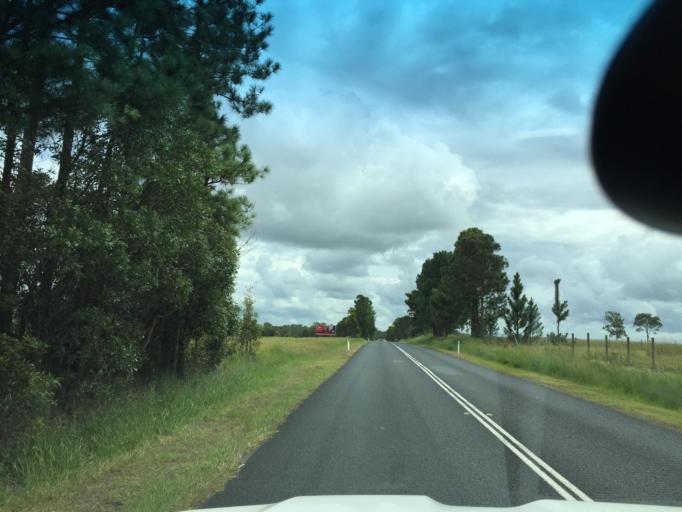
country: AU
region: Queensland
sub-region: Moreton Bay
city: Morayfield
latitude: -27.1156
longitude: 152.9796
